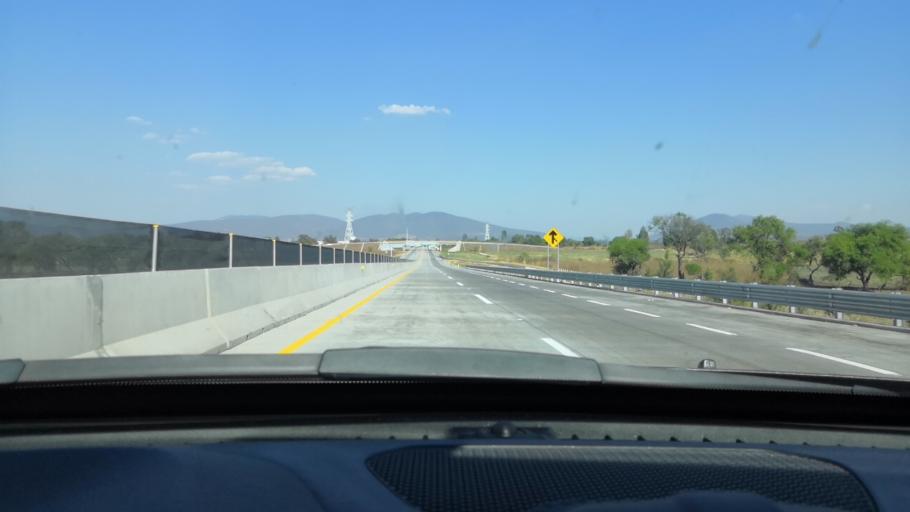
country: MX
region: Jalisco
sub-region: Ixtlahuacan de los Membrillos
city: Los Cedros
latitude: 20.4077
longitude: -103.2288
